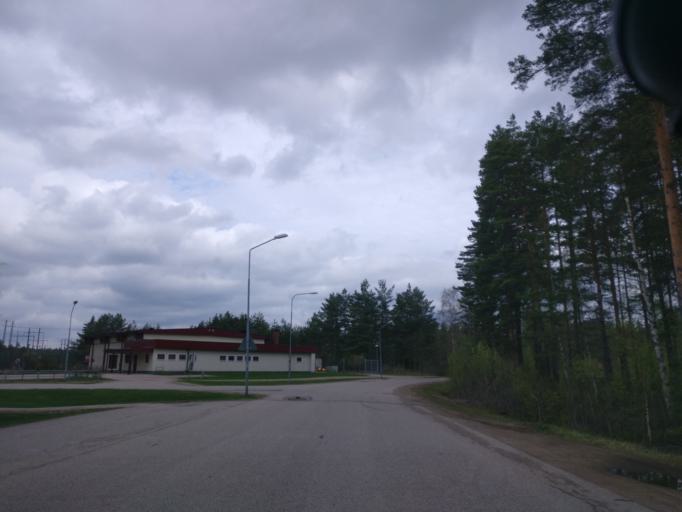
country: SE
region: Vaermland
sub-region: Hagfors Kommun
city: Ekshaerad
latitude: 60.1733
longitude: 13.4861
